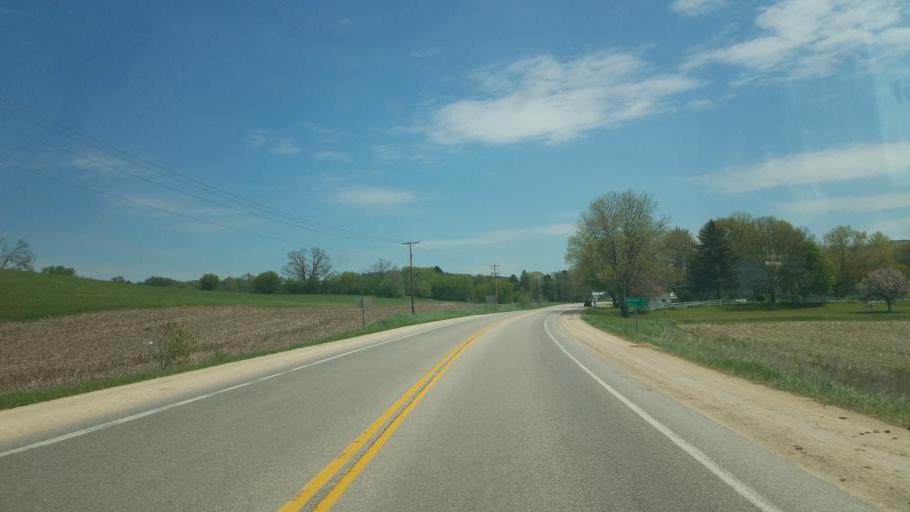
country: US
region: Wisconsin
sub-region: Monroe County
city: Tomah
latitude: 43.8326
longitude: -90.4724
